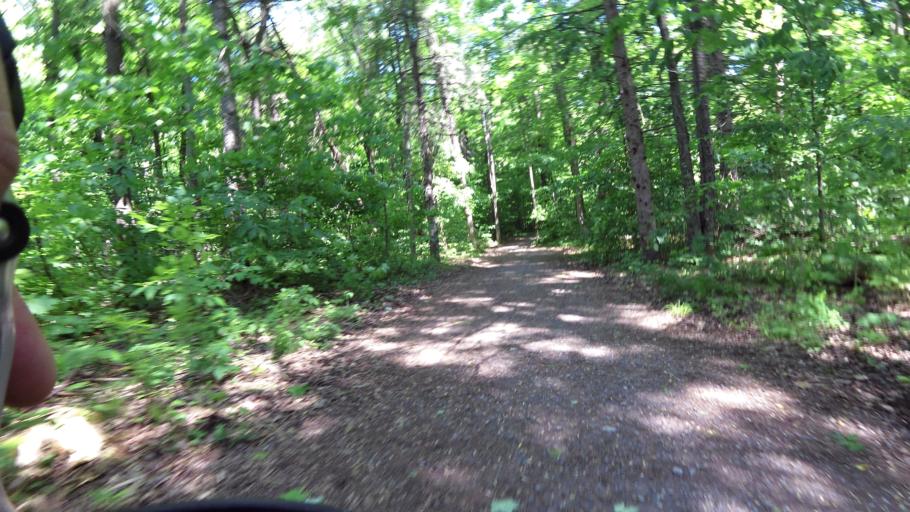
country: CA
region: Quebec
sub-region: Outaouais
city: Wakefield
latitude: 45.5288
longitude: -75.8648
